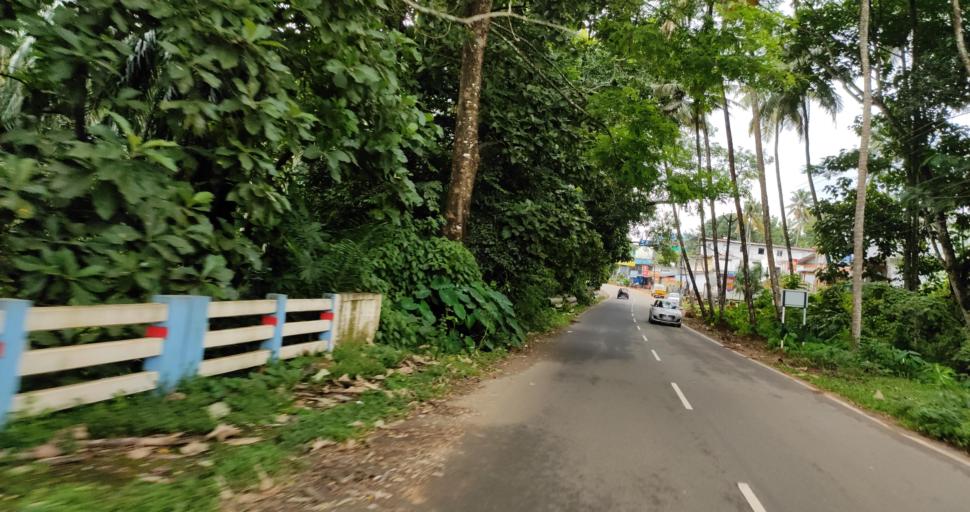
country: IN
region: Kerala
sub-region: Ernakulam
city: Angamali
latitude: 10.2953
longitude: 76.4904
